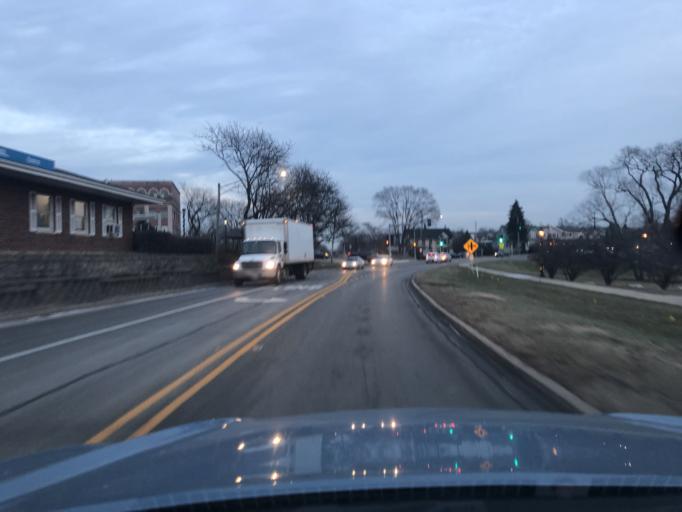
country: US
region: Illinois
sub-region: DuPage County
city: Itasca
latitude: 41.9714
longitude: -88.0144
